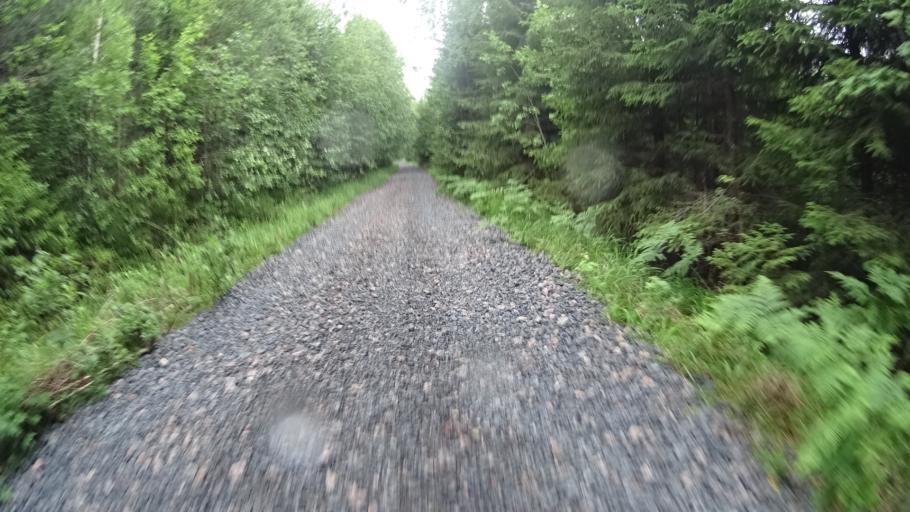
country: FI
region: Uusimaa
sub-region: Helsinki
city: Karkkila
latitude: 60.5871
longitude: 24.1530
